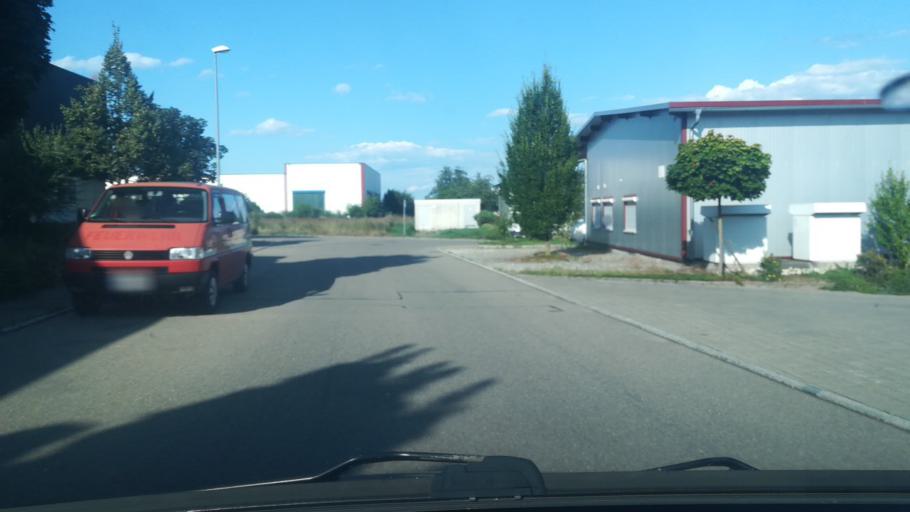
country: DE
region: Baden-Wuerttemberg
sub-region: Tuebingen Region
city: Sickenhausen
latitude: 48.5442
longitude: 9.1733
